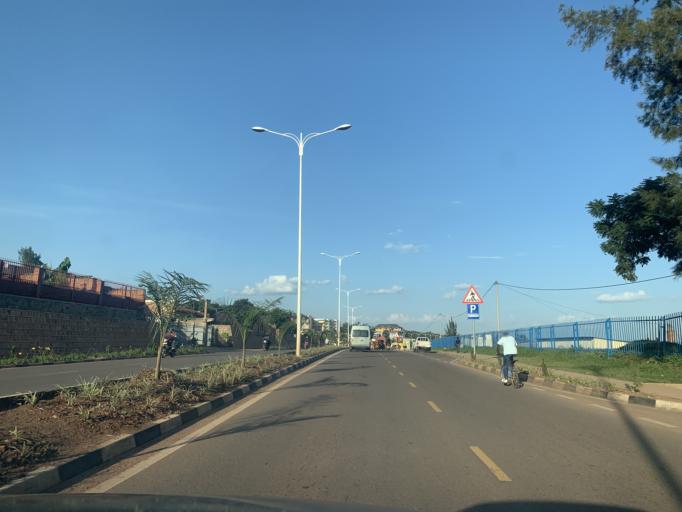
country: RW
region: Kigali
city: Kigali
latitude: -1.9637
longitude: 30.1081
